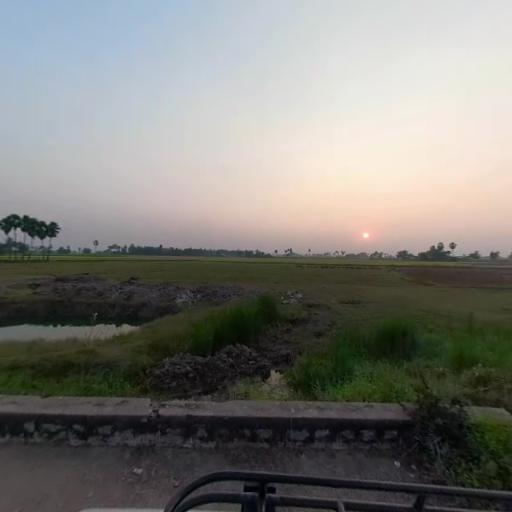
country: IN
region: Telangana
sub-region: Nalgonda
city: Suriapet
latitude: 17.0757
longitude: 79.5488
